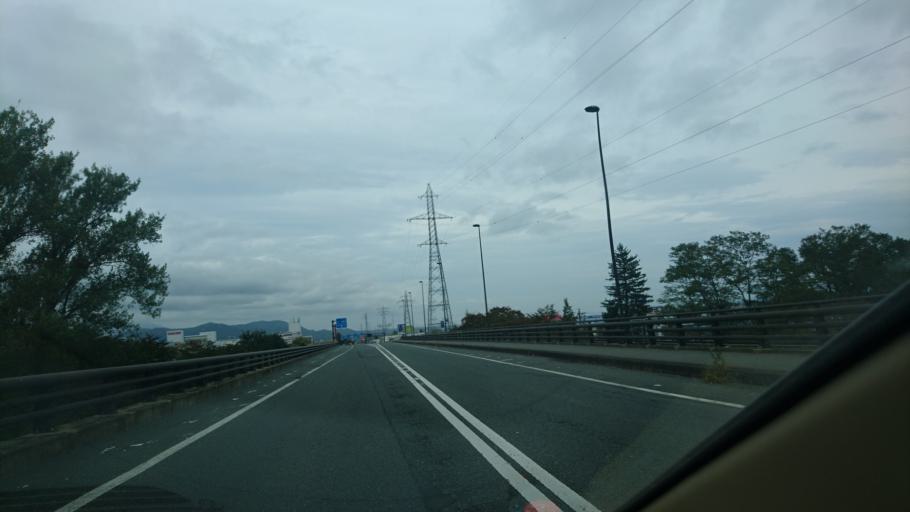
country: JP
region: Iwate
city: Morioka-shi
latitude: 39.7067
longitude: 141.1017
